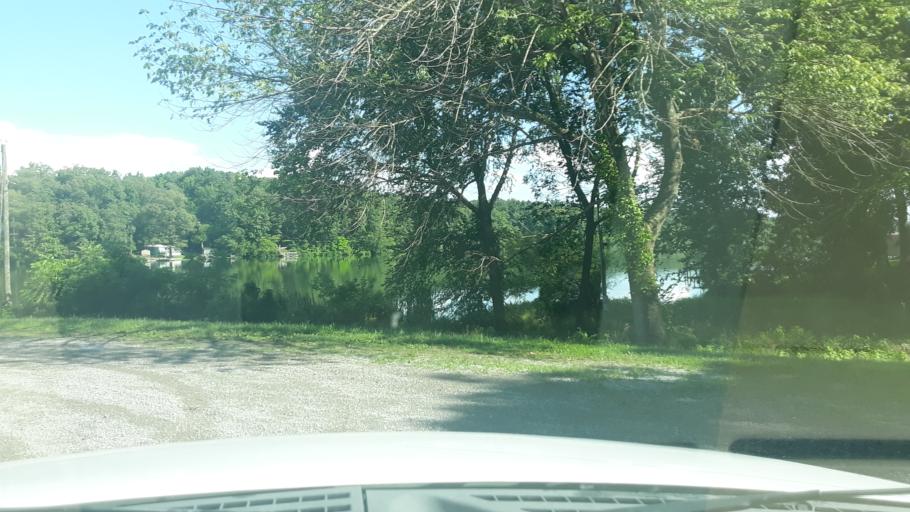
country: US
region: Illinois
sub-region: Saline County
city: Harrisburg
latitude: 37.8526
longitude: -88.5870
